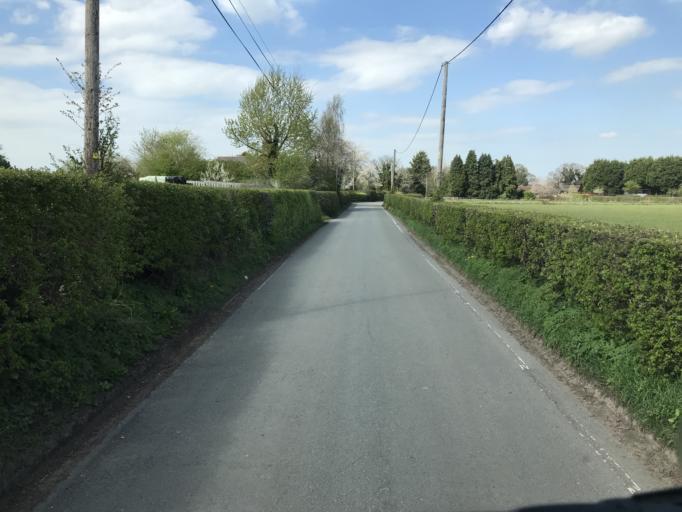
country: GB
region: England
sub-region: Cheshire West and Chester
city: Tarvin
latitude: 53.2060
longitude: -2.7652
